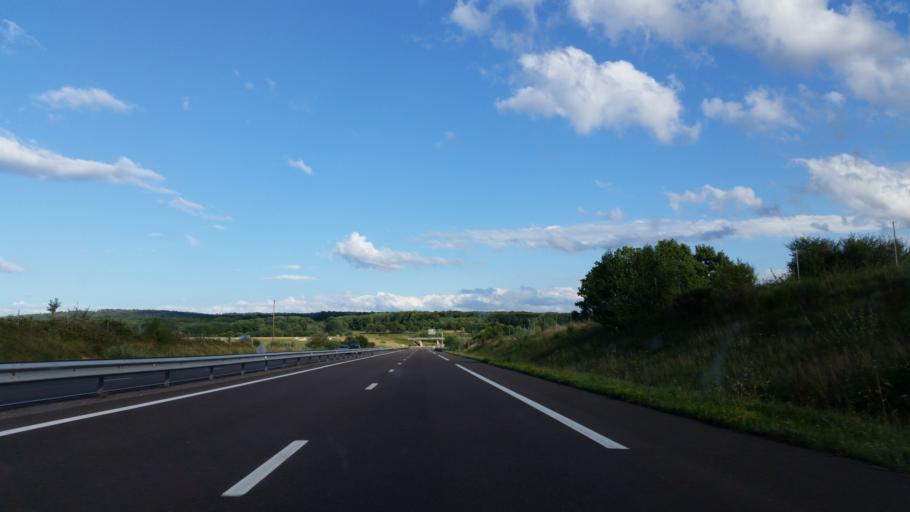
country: FR
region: Franche-Comte
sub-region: Departement de la Haute-Saone
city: Roye
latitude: 47.6527
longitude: 6.5823
